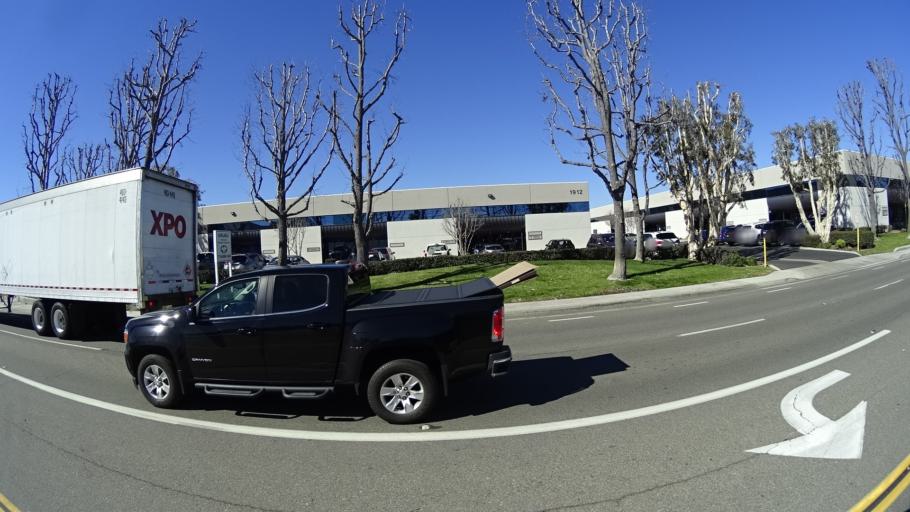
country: US
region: California
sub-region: Orange County
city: Orange
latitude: 33.8194
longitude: -117.8620
